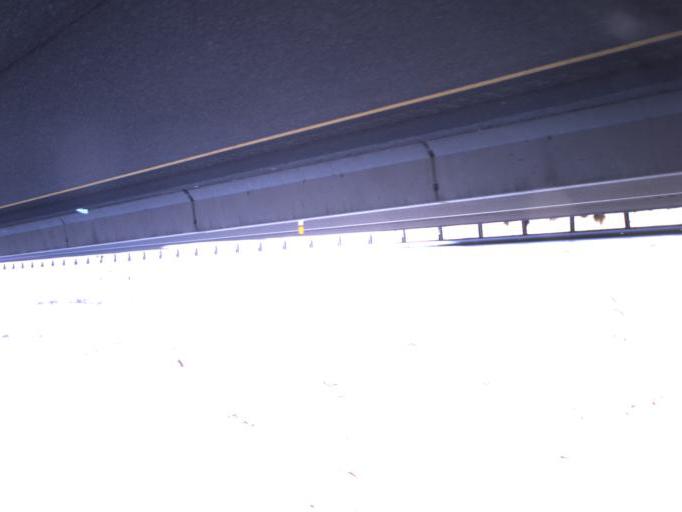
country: US
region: Utah
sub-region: Carbon County
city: East Carbon City
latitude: 38.9212
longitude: -110.4391
